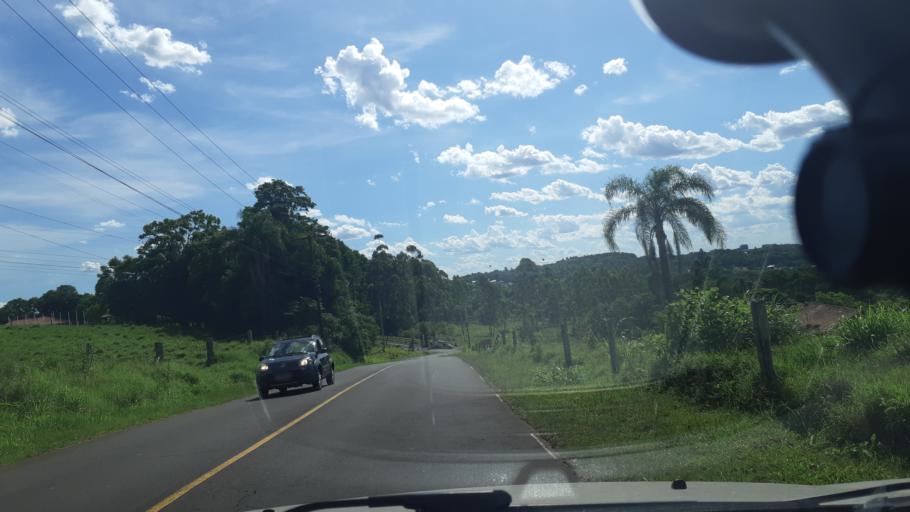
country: BR
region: Rio Grande do Sul
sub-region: Novo Hamburgo
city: Novo Hamburgo
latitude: -29.6268
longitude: -51.1054
